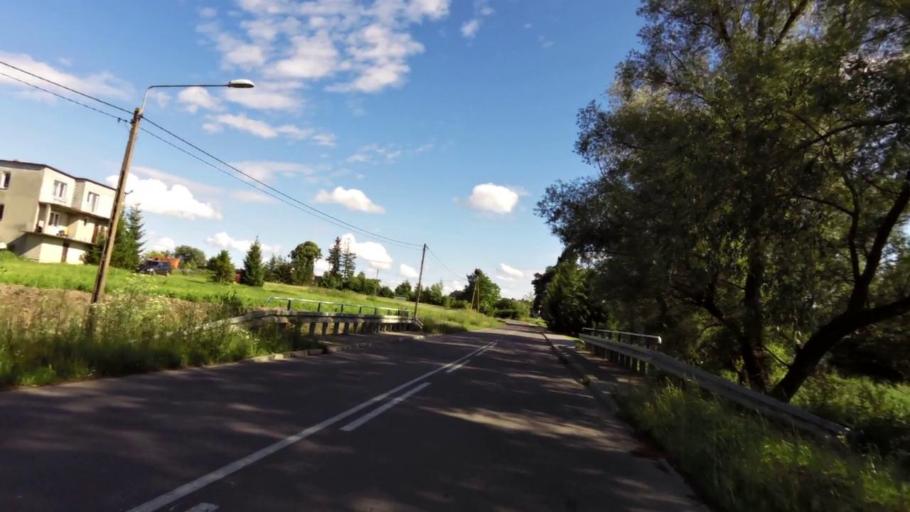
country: PL
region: West Pomeranian Voivodeship
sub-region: Powiat slawienski
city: Slawno
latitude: 54.4577
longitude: 16.7378
